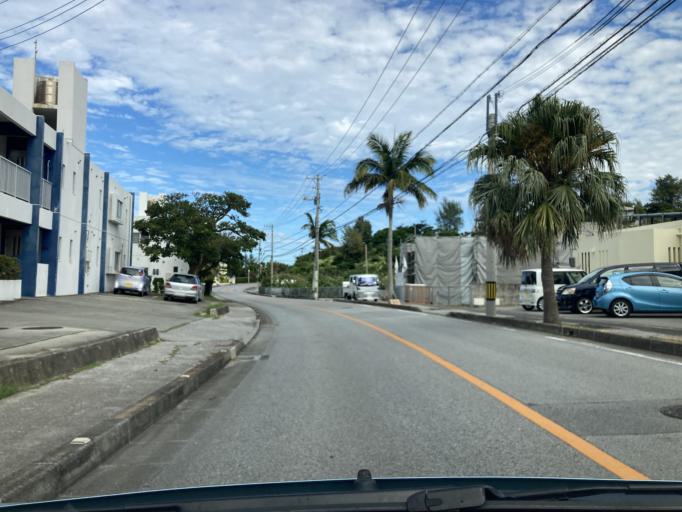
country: JP
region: Okinawa
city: Ishikawa
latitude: 26.4324
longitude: 127.7595
